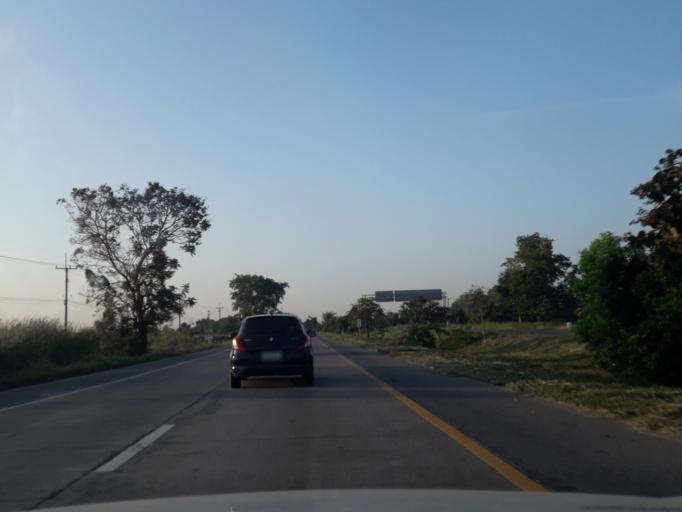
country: TH
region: Phra Nakhon Si Ayutthaya
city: Phra Nakhon Si Ayutthaya
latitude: 14.2982
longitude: 100.5250
